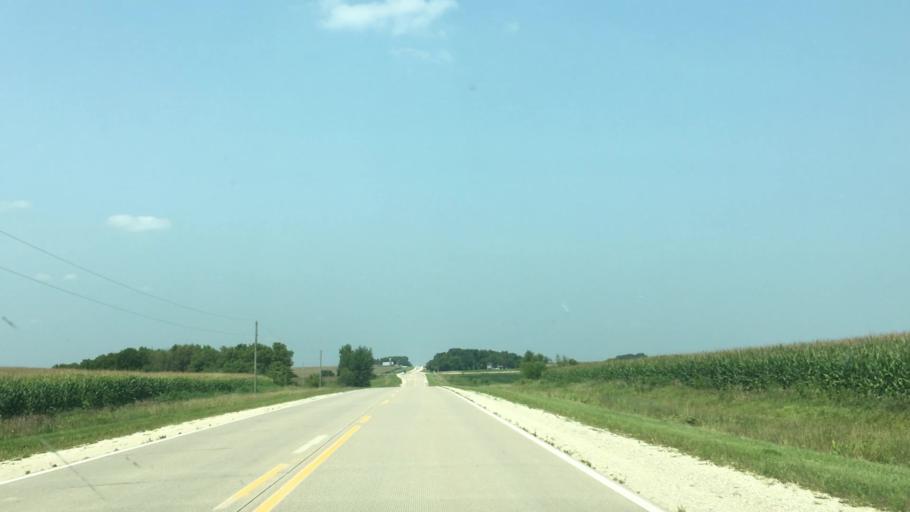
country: US
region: Iowa
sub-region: Fayette County
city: Fayette
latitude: 42.7541
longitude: -91.8043
